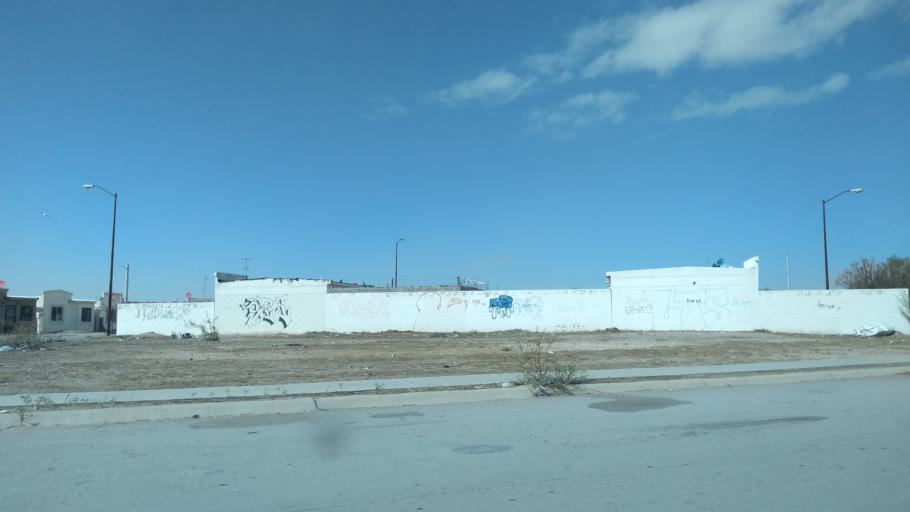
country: US
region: Texas
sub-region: El Paso County
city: San Elizario
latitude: 31.5741
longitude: -106.3290
